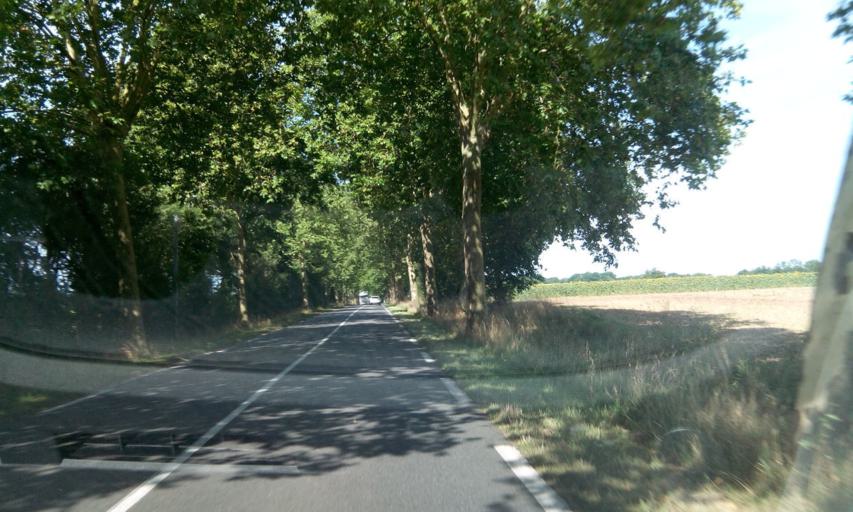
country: FR
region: Poitou-Charentes
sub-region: Departement de la Vienne
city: Charroux
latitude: 46.1405
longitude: 0.4274
